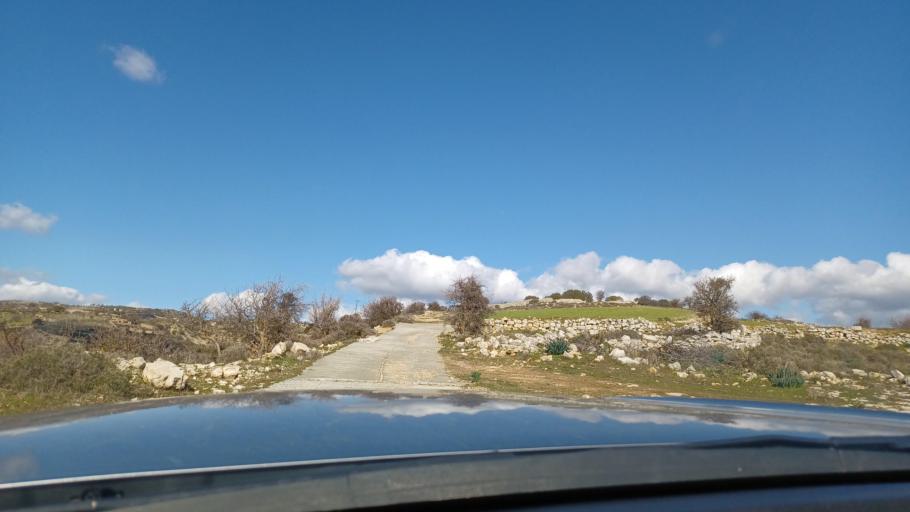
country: CY
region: Limassol
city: Pachna
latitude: 34.8187
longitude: 32.7900
